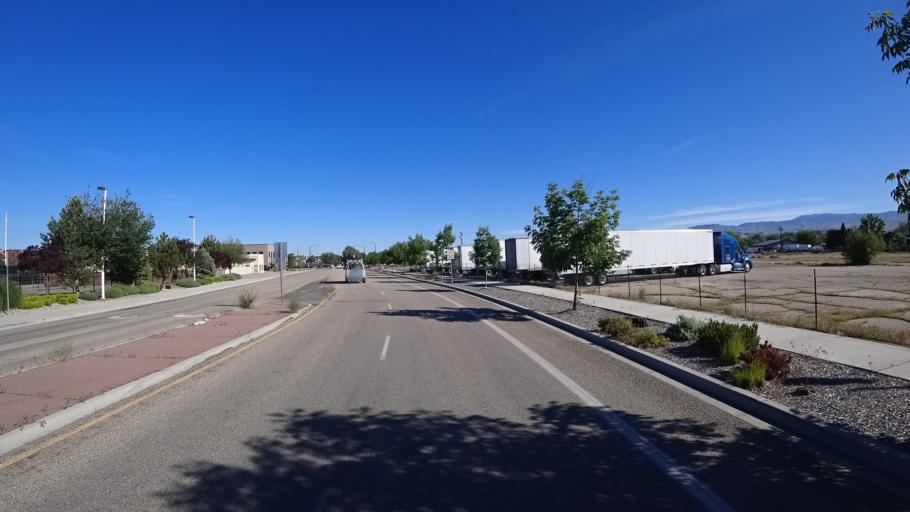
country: US
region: Idaho
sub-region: Ada County
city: Garden City
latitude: 43.6204
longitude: -116.2265
